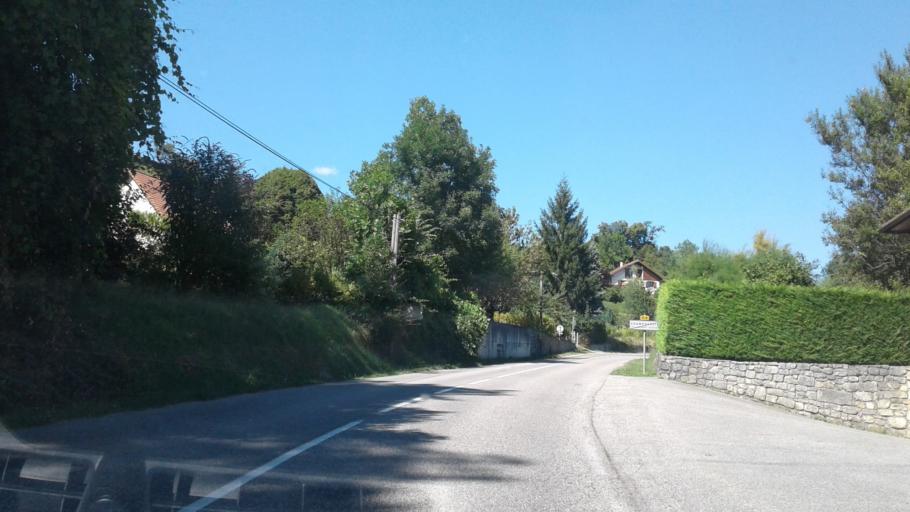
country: FR
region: Rhone-Alpes
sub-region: Departement de l'Ain
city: Artemare
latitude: 45.8772
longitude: 5.6635
